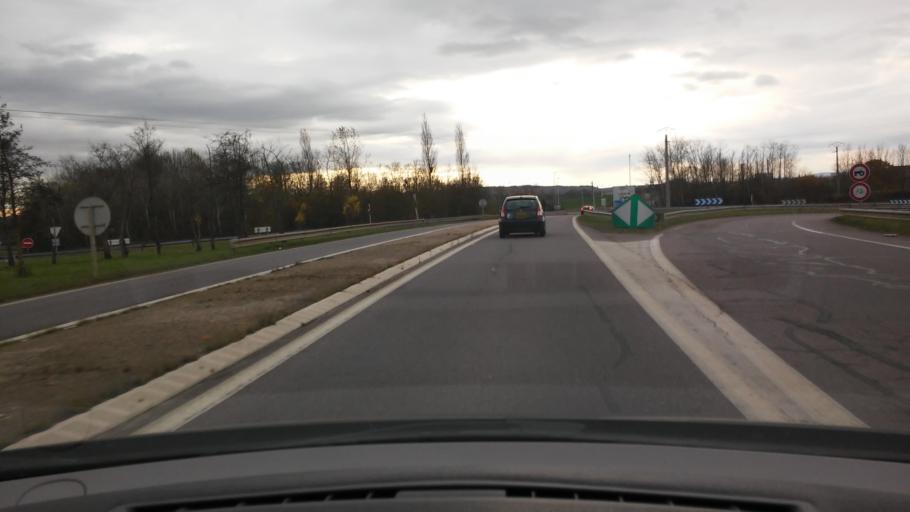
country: FR
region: Lorraine
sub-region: Departement de la Moselle
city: Argancy
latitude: 49.1991
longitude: 6.2088
